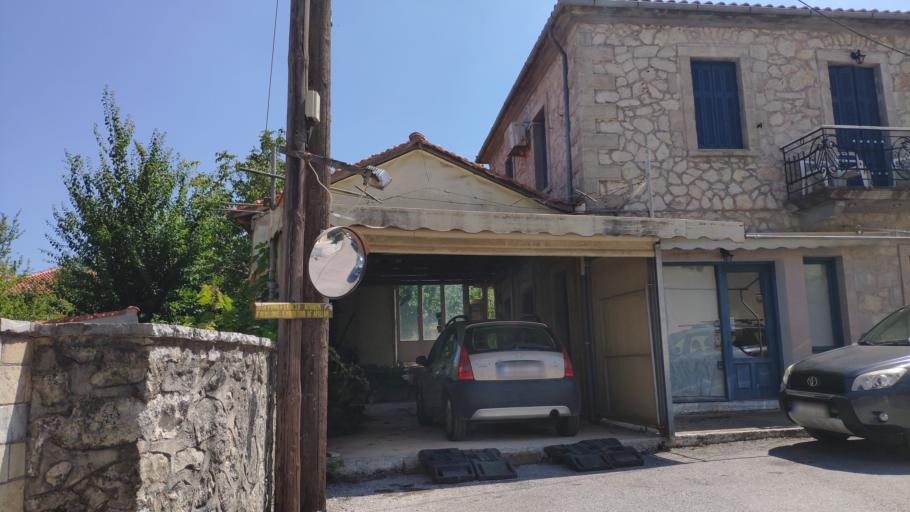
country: GR
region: Ionian Islands
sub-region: Lefkada
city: Nidri
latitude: 38.7588
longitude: 20.6491
